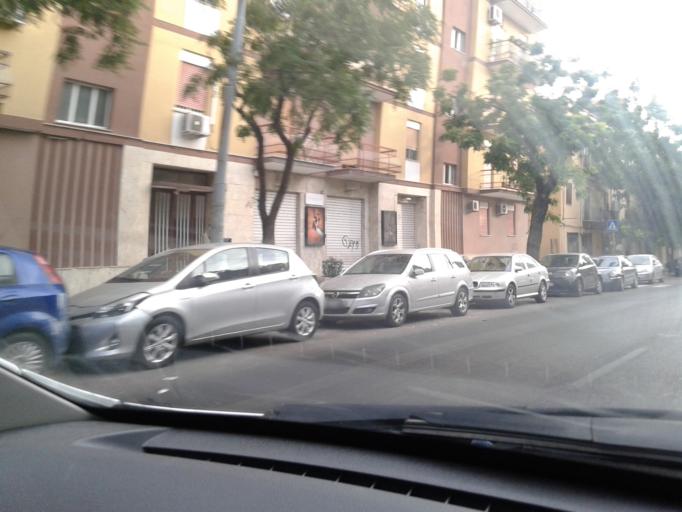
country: IT
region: Sicily
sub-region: Palermo
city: Palermo
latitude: 38.1003
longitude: 13.3235
